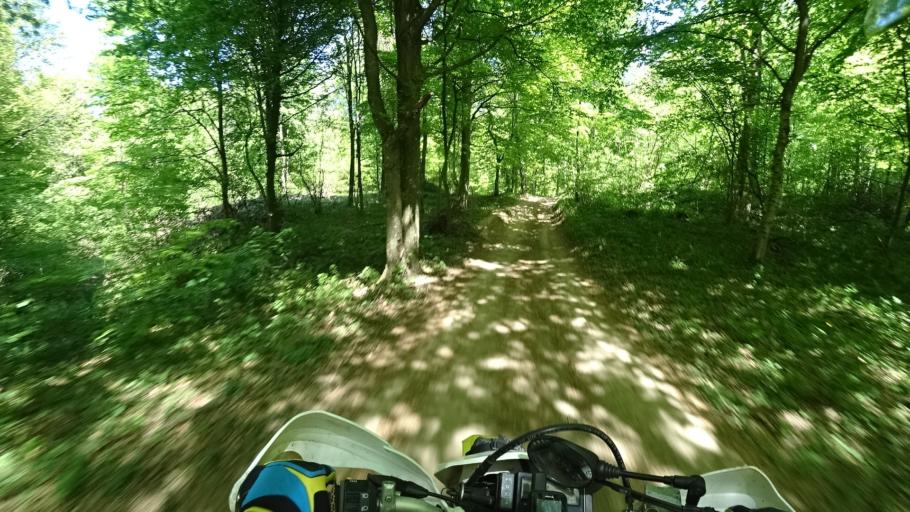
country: HR
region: Zagrebacka
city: Jablanovec
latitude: 45.8679
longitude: 15.8579
